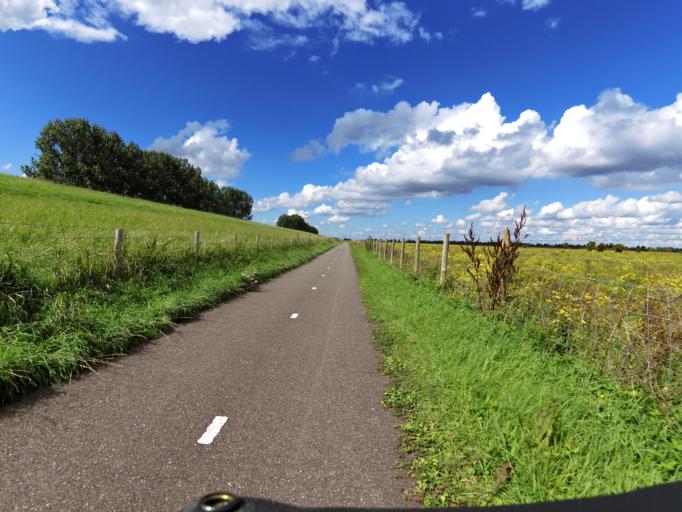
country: NL
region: North Brabant
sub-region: Gemeente Steenbergen
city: Dinteloord
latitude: 51.6884
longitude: 4.3572
